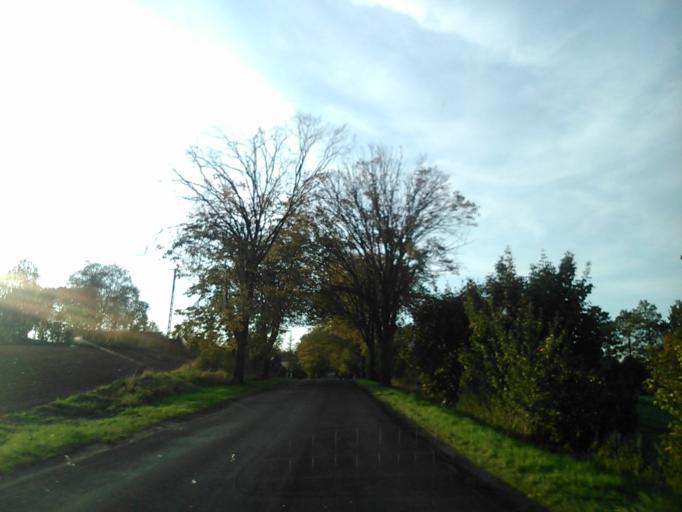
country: PL
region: Kujawsko-Pomorskie
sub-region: Powiat wabrzeski
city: Debowa Laka
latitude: 53.2486
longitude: 19.1253
